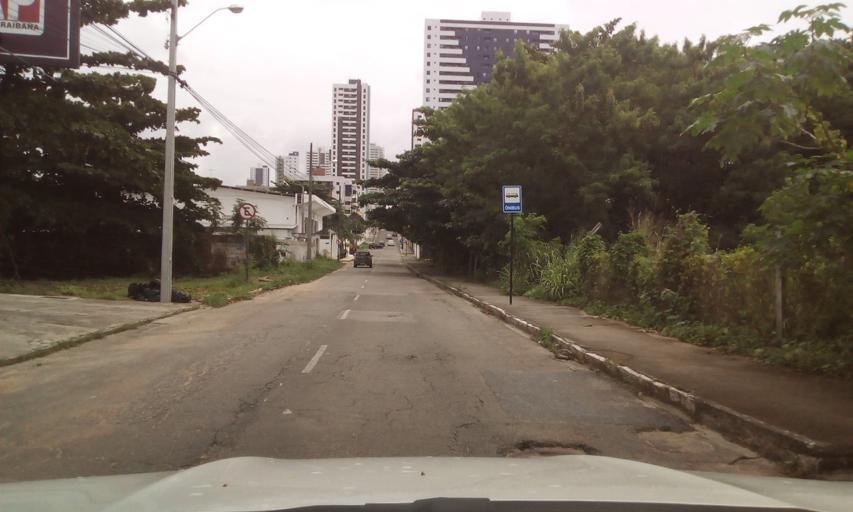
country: BR
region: Paraiba
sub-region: Joao Pessoa
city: Joao Pessoa
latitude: -7.1135
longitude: -34.8443
